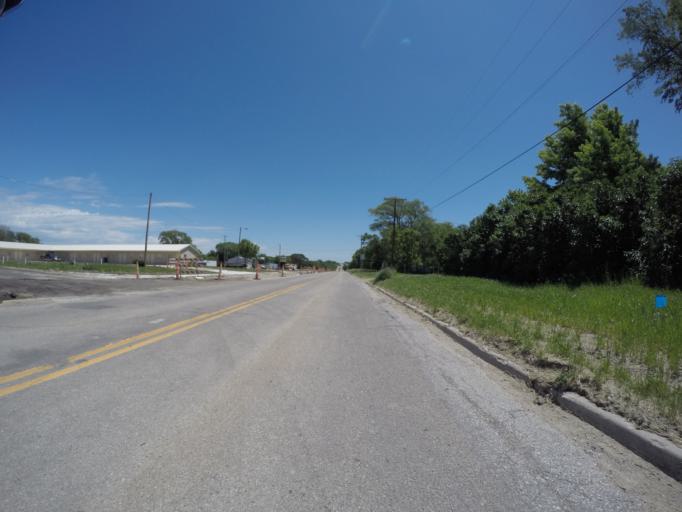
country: US
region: Kansas
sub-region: Jewell County
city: Mankato
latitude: 39.7848
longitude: -98.2219
